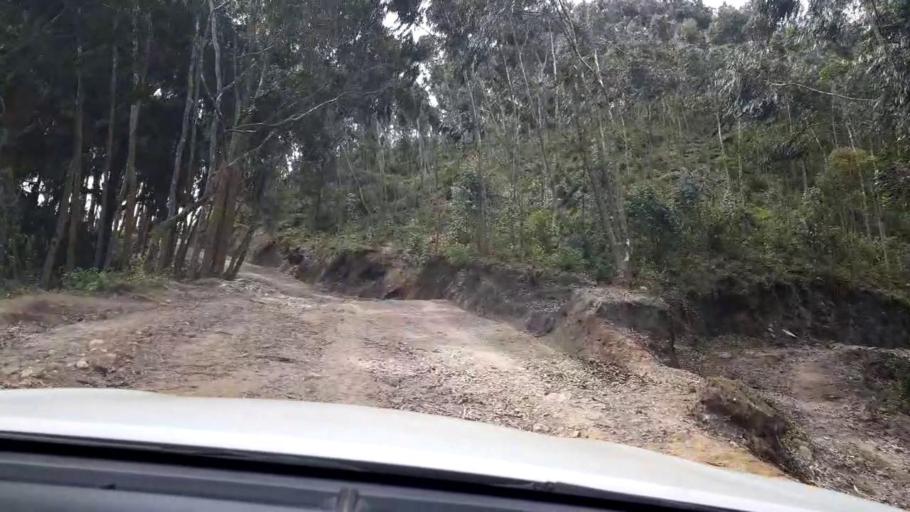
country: RW
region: Western Province
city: Kibuye
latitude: -1.8724
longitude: 29.4522
